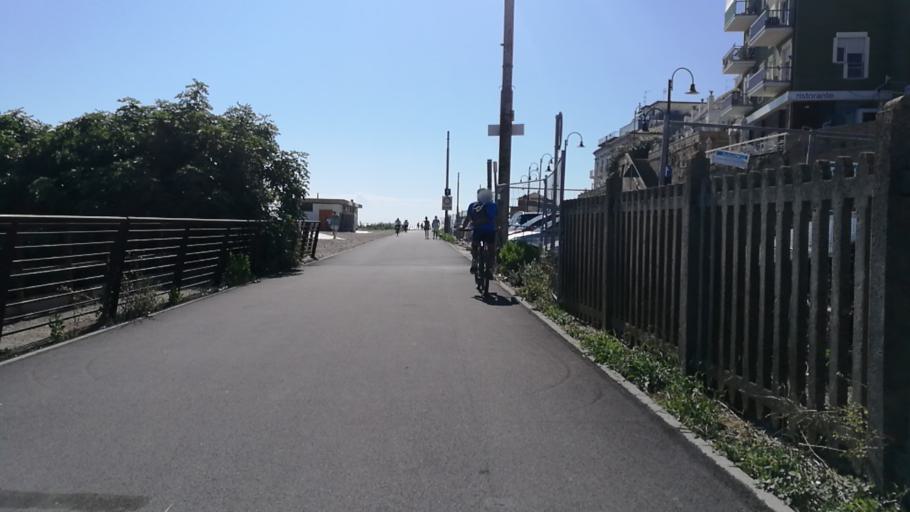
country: IT
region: Abruzzo
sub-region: Provincia di Chieti
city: Marina di San Vito
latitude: 42.3084
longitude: 14.4459
